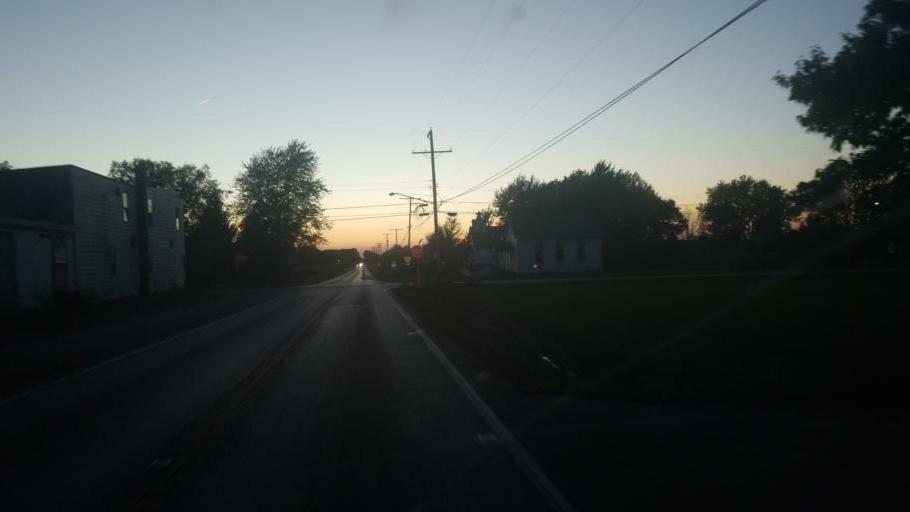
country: US
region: Ohio
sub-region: Ashtabula County
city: Jefferson
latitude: 41.7517
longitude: -80.6669
